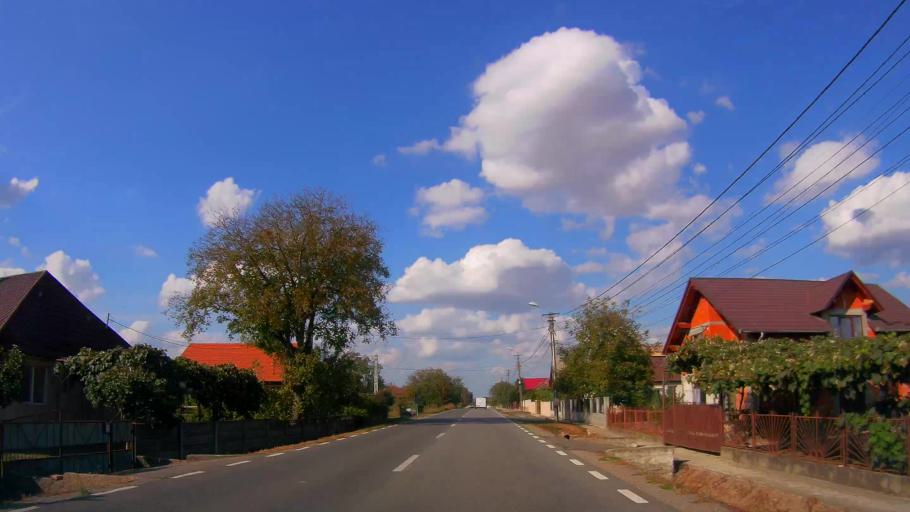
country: RO
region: Satu Mare
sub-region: Comuna Turulung
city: Draguseni
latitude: 47.8952
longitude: 23.0743
